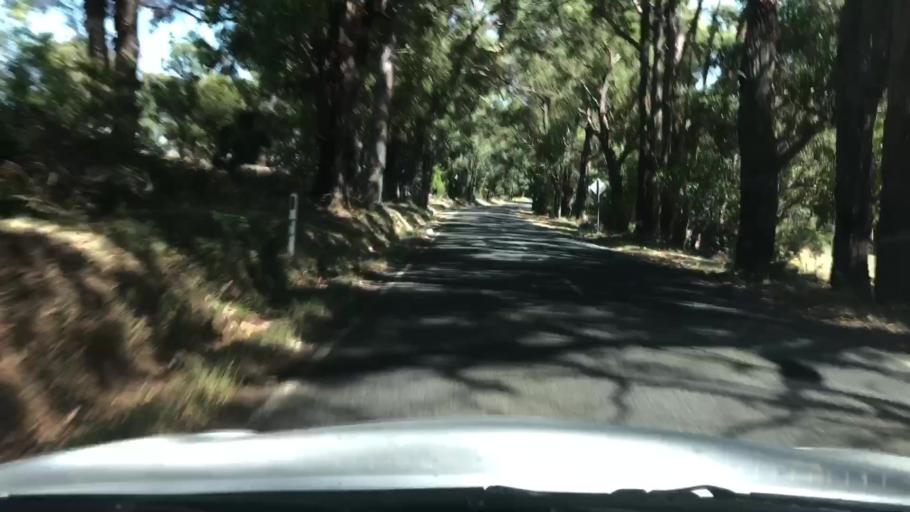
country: AU
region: Victoria
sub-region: Yarra Ranges
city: Macclesfield
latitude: -37.8674
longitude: 145.4794
